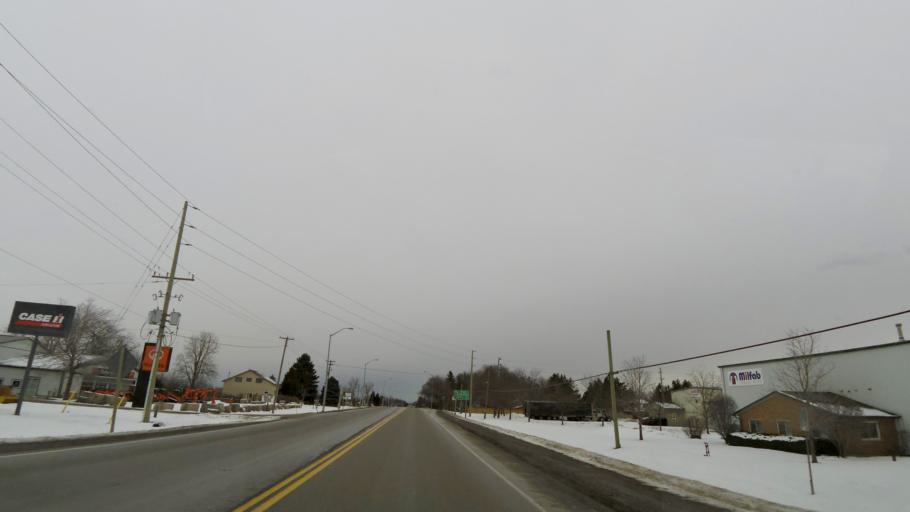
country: CA
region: Ontario
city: Ancaster
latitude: 43.2959
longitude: -79.9809
